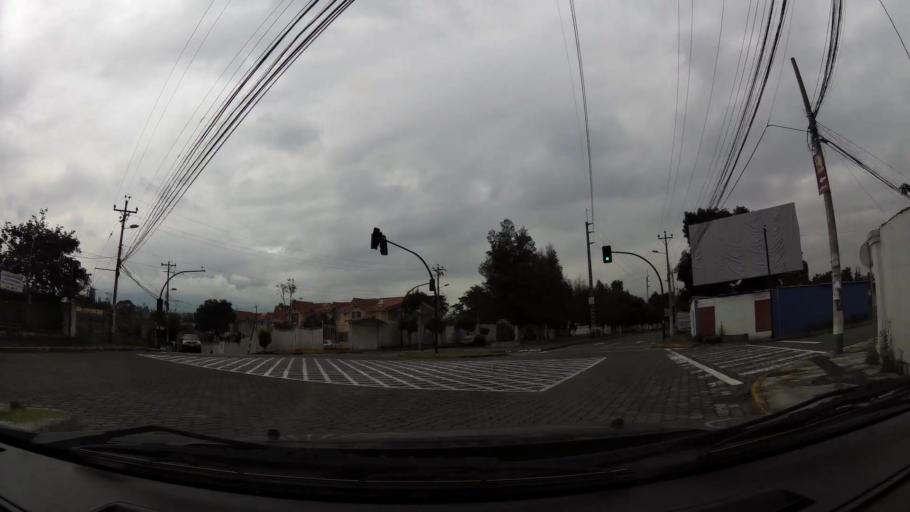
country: EC
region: Pichincha
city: Sangolqui
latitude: -0.3092
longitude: -78.4559
